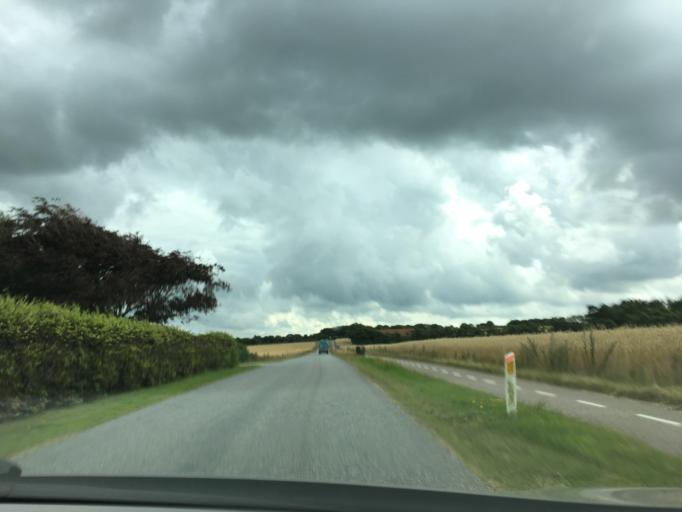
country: DK
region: South Denmark
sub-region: Varde Kommune
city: Oksbol
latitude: 55.7293
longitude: 8.2674
